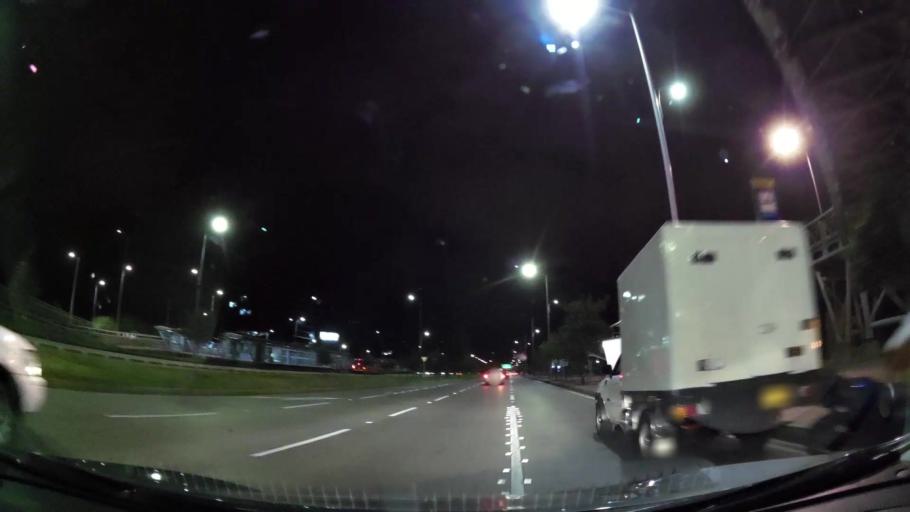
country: CO
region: Bogota D.C.
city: Bogota
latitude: 4.6746
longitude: -74.1164
